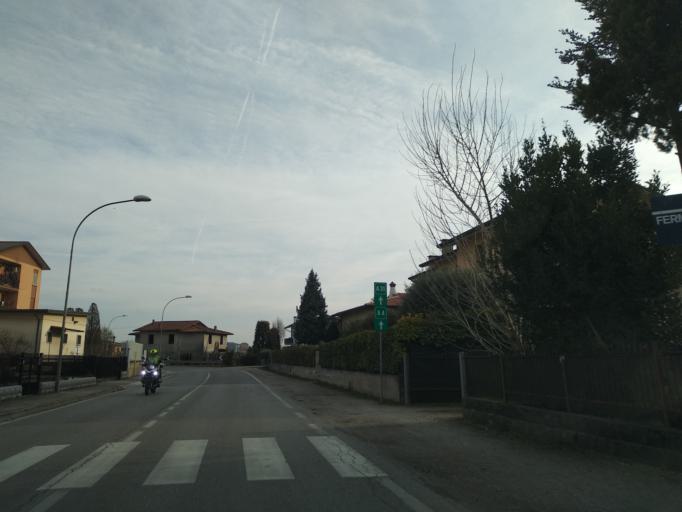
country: IT
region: Veneto
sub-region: Provincia di Vicenza
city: Ponte di Barbarano
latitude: 45.3935
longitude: 11.5701
